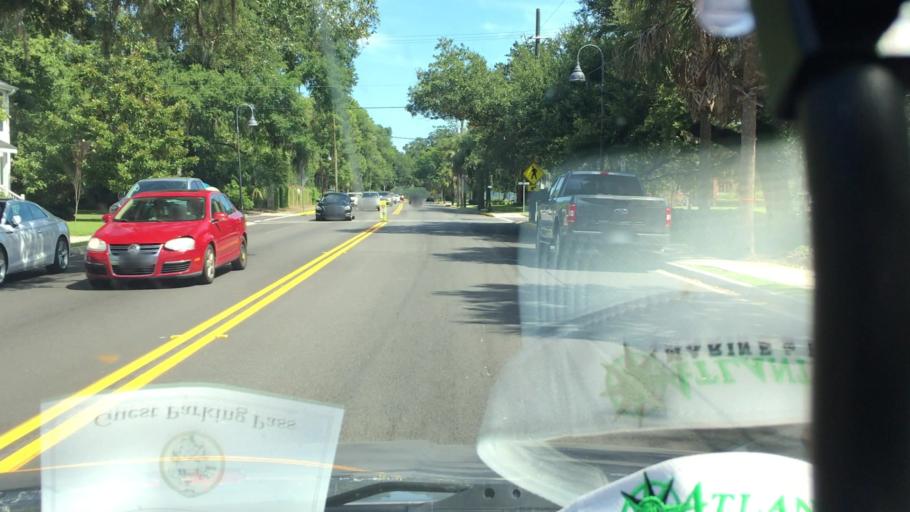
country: US
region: South Carolina
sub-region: Beaufort County
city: Beaufort
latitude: 32.4365
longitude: -80.6699
